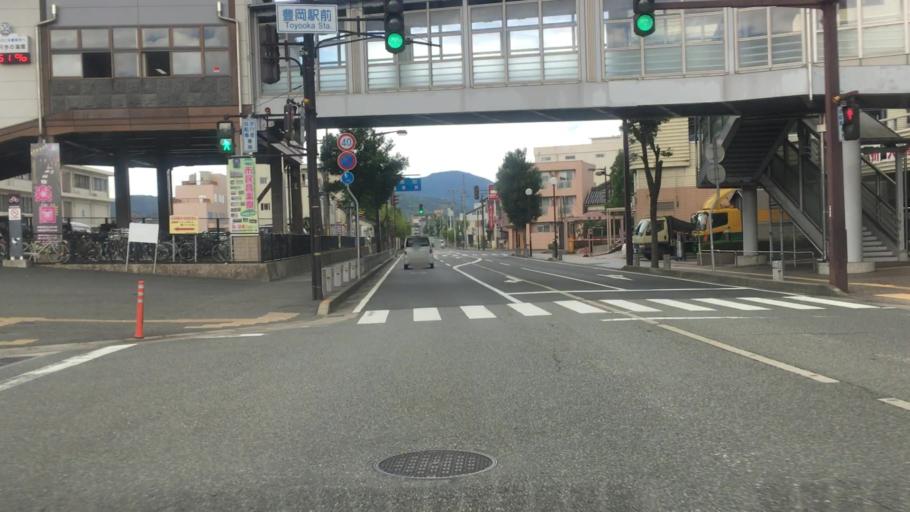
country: JP
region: Hyogo
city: Toyooka
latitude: 35.5441
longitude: 134.8144
